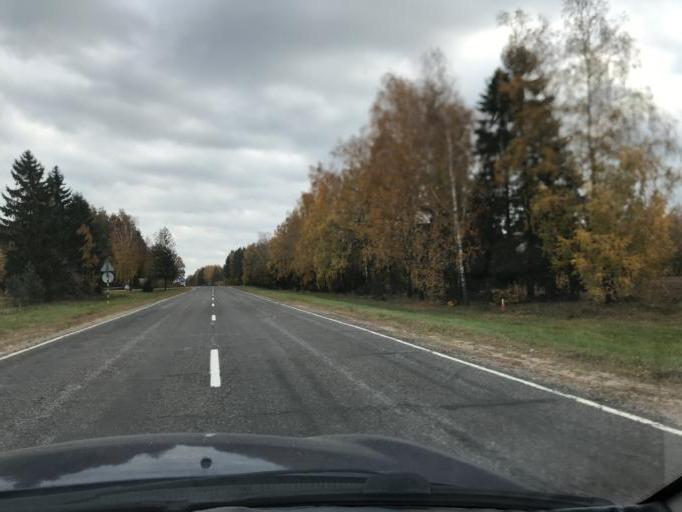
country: BY
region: Grodnenskaya
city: Lida
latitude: 53.7519
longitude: 25.2209
